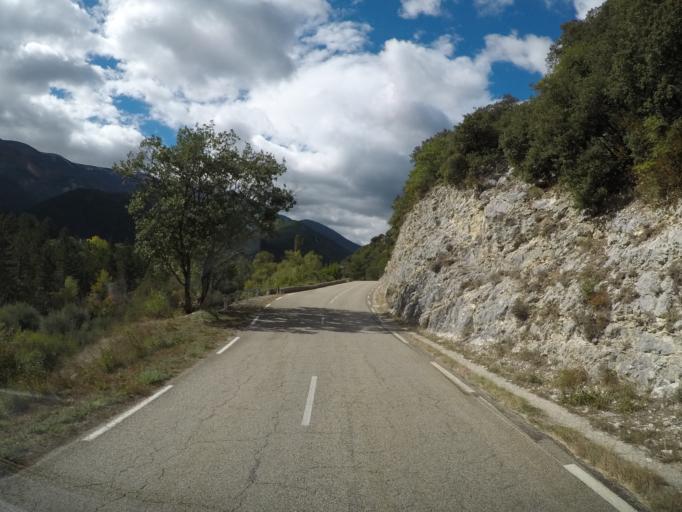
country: FR
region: Provence-Alpes-Cote d'Azur
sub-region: Departement du Vaucluse
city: Sault
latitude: 44.1843
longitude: 5.3585
